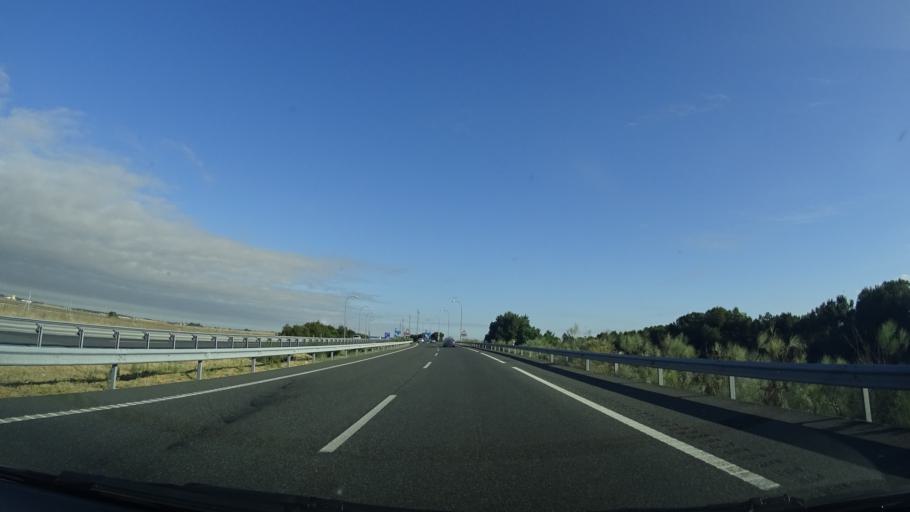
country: ES
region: Castille and Leon
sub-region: Provincia de Avila
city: Sanchidrian
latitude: 40.8771
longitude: -4.5676
